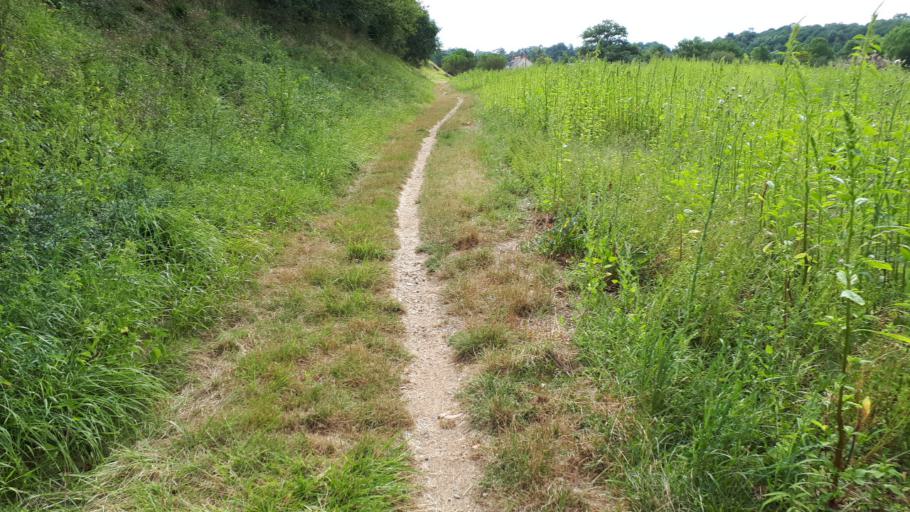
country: FR
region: Pays de la Loire
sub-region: Departement de Maine-et-Loire
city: Rochefort-sur-Loire
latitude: 47.3311
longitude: -0.6886
